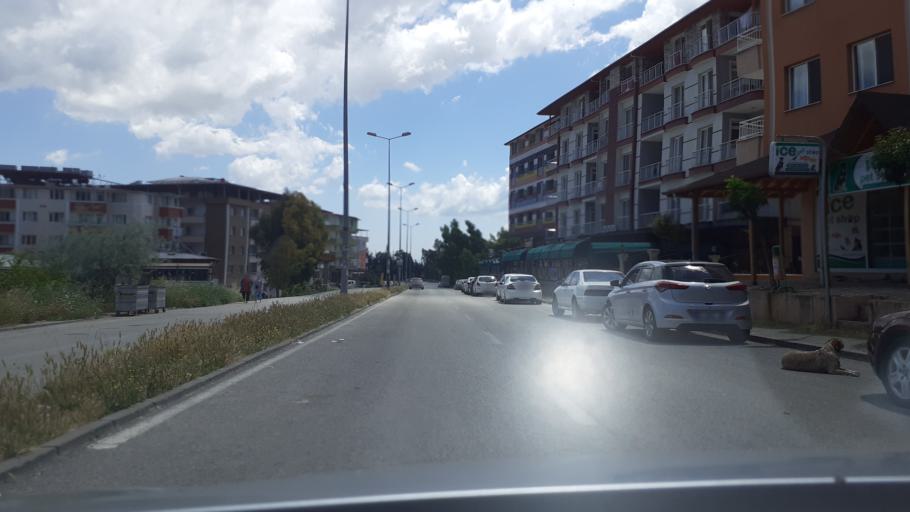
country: TR
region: Hatay
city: Anayazi
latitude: 36.3348
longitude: 36.2025
